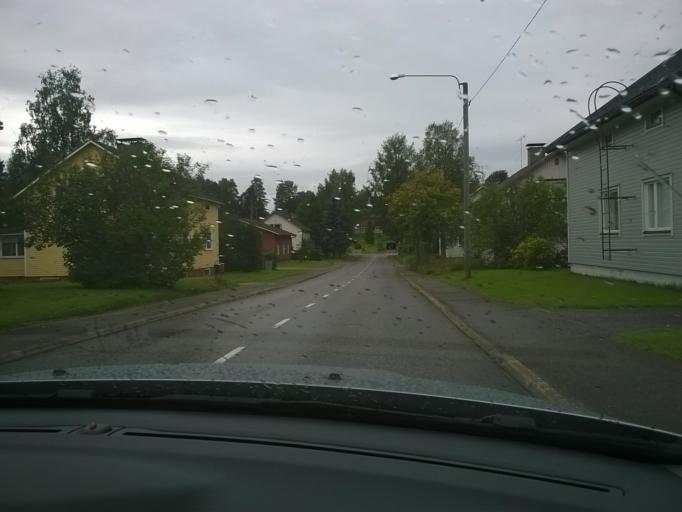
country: FI
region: Kainuu
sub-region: Kehys-Kainuu
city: Kuhmo
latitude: 64.1244
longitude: 29.5177
